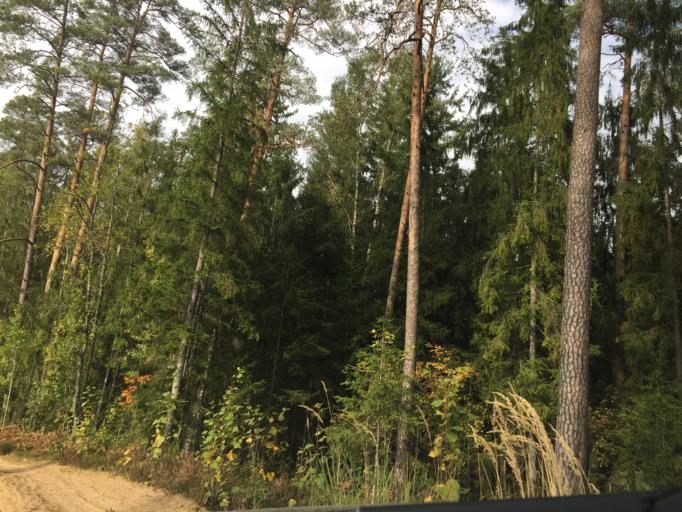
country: LV
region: Garkalne
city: Garkalne
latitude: 56.9464
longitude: 24.4319
